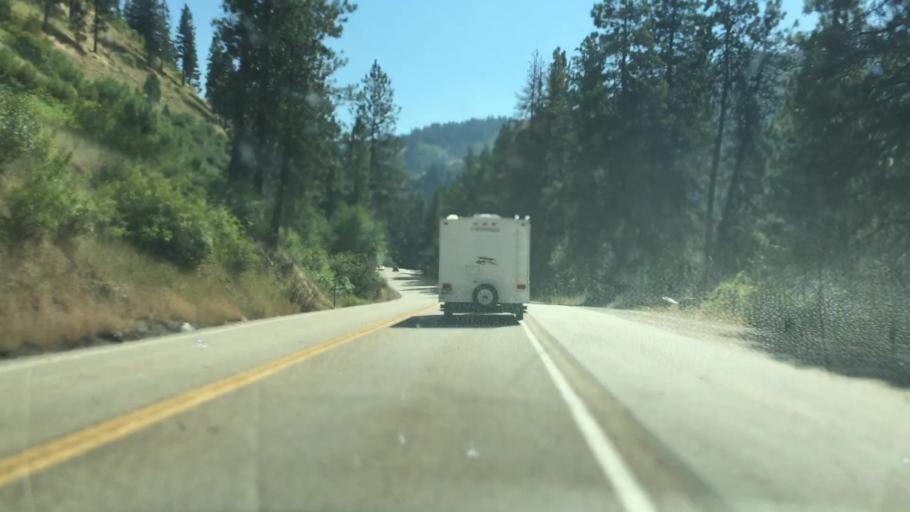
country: US
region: Idaho
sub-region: Boise County
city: Idaho City
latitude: 44.0607
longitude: -116.1242
